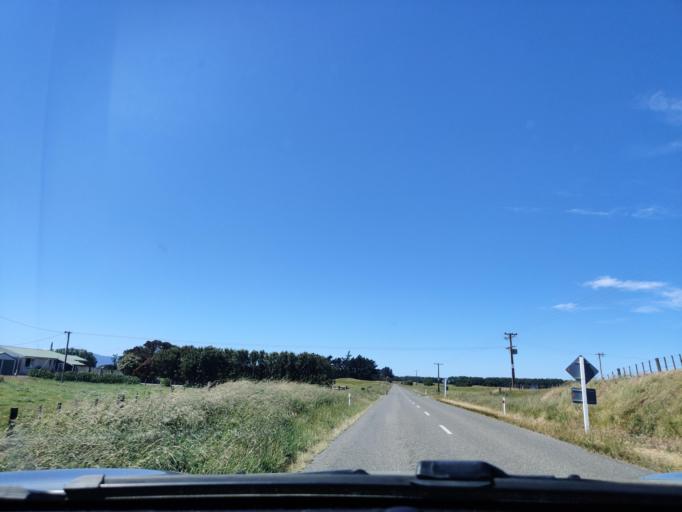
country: NZ
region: Wellington
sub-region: Upper Hutt City
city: Upper Hutt
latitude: -41.2721
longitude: 175.2674
